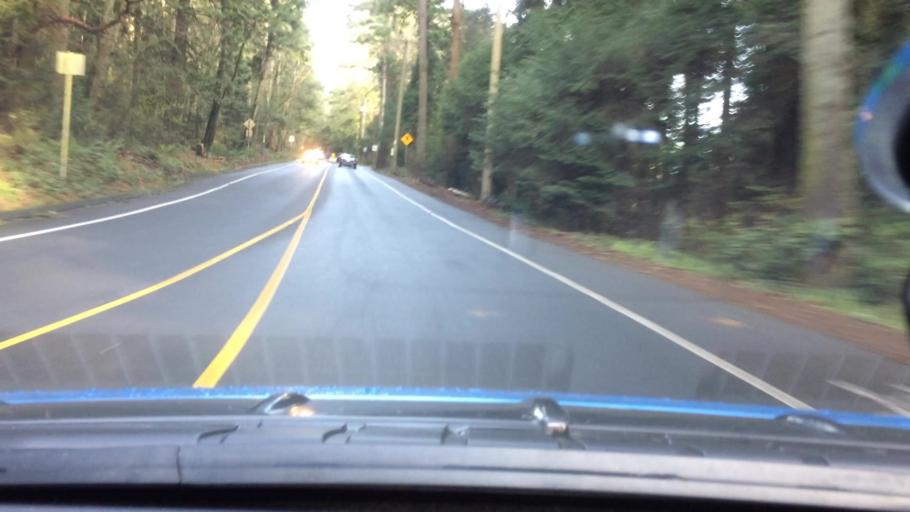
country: CA
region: British Columbia
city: Oak Bay
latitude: 48.4953
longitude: -123.3355
